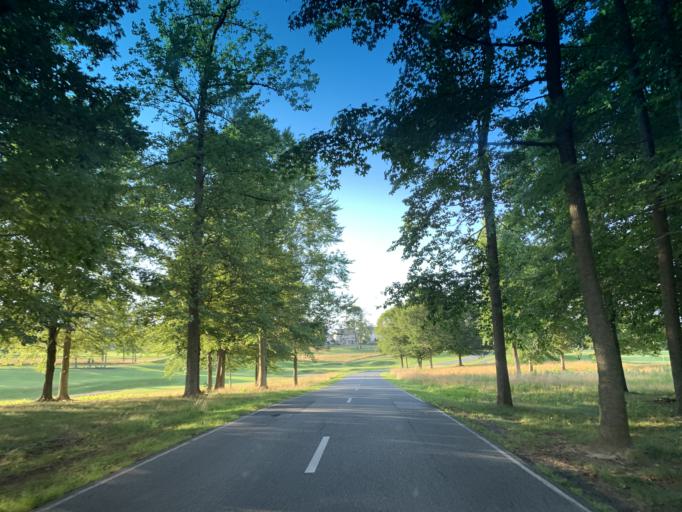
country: US
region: Maryland
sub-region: Harford County
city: Havre de Grace
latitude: 39.5398
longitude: -76.1333
